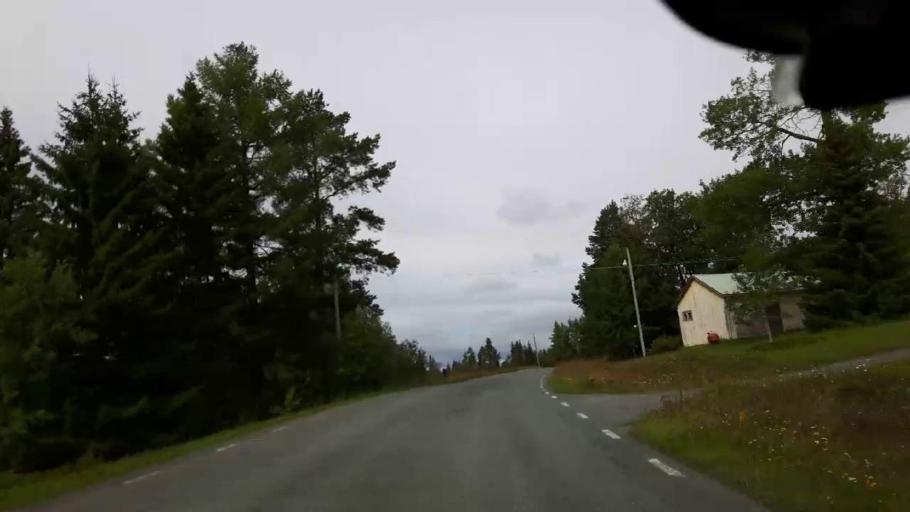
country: SE
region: Jaemtland
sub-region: Krokoms Kommun
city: Valla
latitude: 63.4545
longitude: 14.0452
